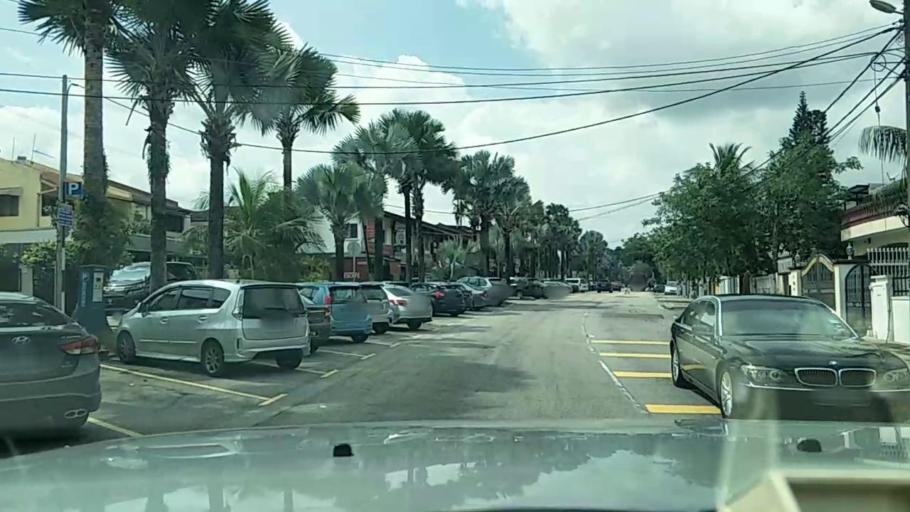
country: MY
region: Kuala Lumpur
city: Kuala Lumpur
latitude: 3.1312
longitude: 101.6733
